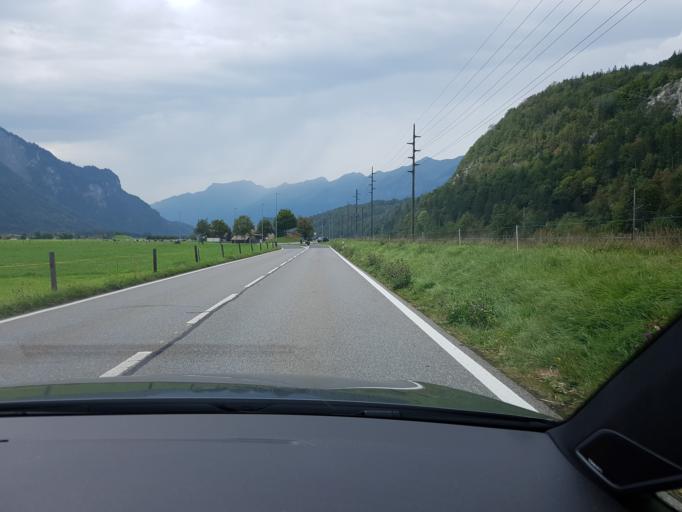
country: CH
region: Obwalden
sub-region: Obwalden
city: Lungern
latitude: 46.7448
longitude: 8.1189
